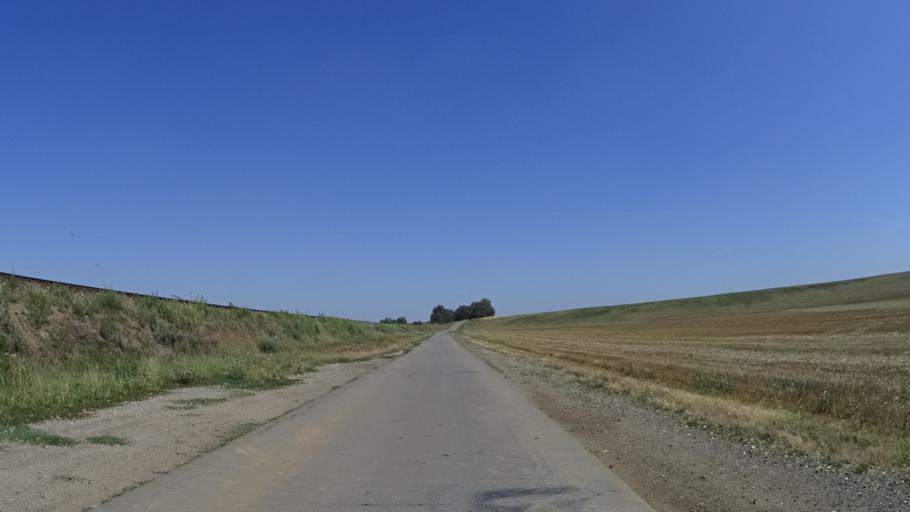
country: CZ
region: South Moravian
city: Petrov
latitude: 48.8834
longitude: 17.2860
